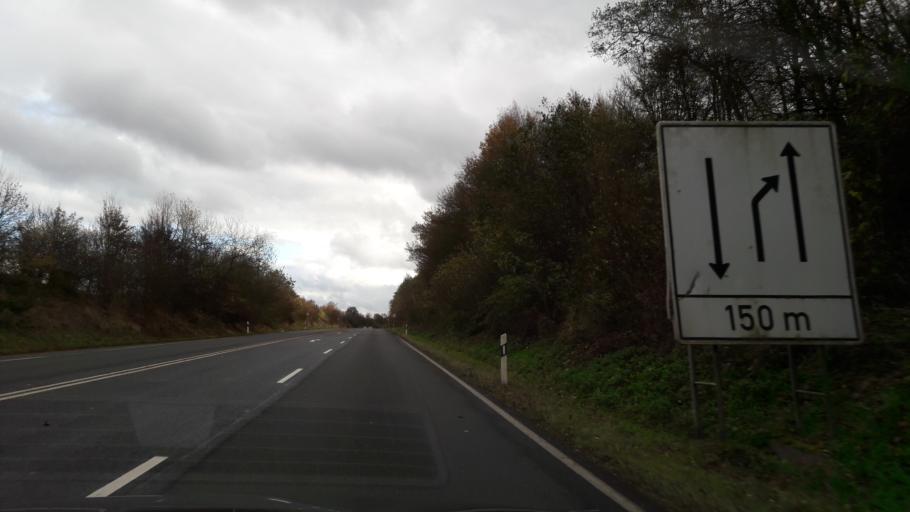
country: DE
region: Rheinland-Pfalz
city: Fell
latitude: 49.7650
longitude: 6.7603
